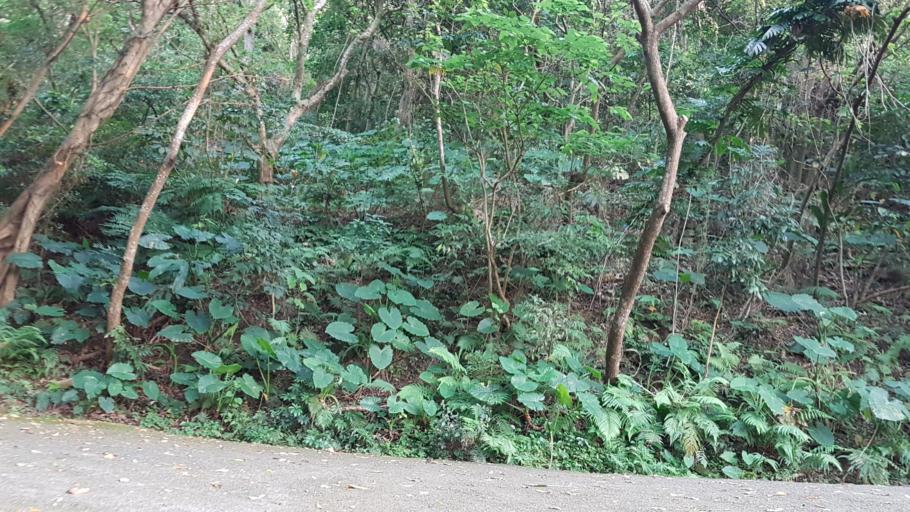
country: TW
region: Taipei
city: Taipei
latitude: 25.0178
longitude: 121.5537
